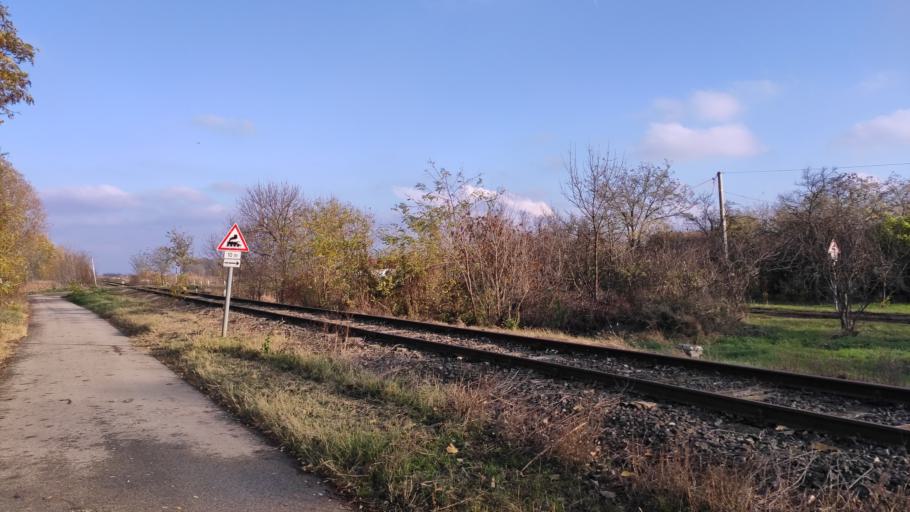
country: HU
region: Bekes
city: Mezobereny
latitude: 46.7645
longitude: 21.0437
